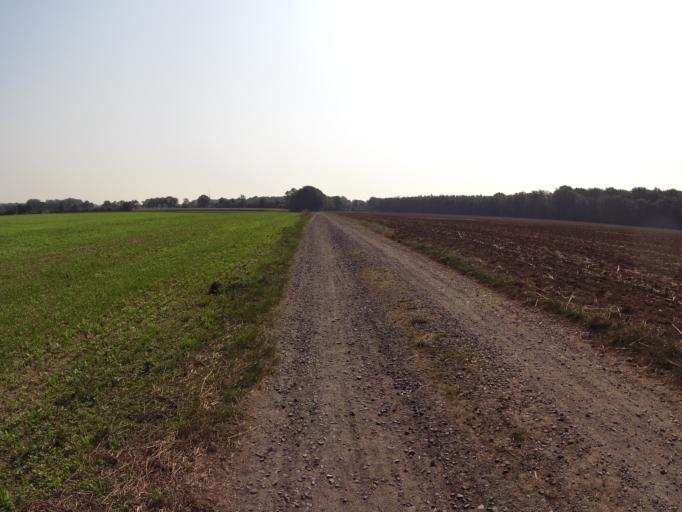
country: DE
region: North Rhine-Westphalia
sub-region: Regierungsbezirk Munster
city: Havixbeck
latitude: 51.9769
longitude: 7.4904
